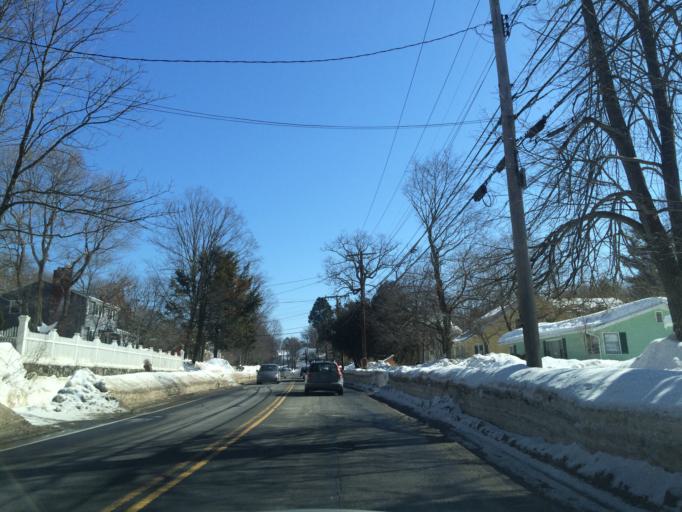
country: US
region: Massachusetts
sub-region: Norfolk County
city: Needham
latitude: 42.2811
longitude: -71.2485
